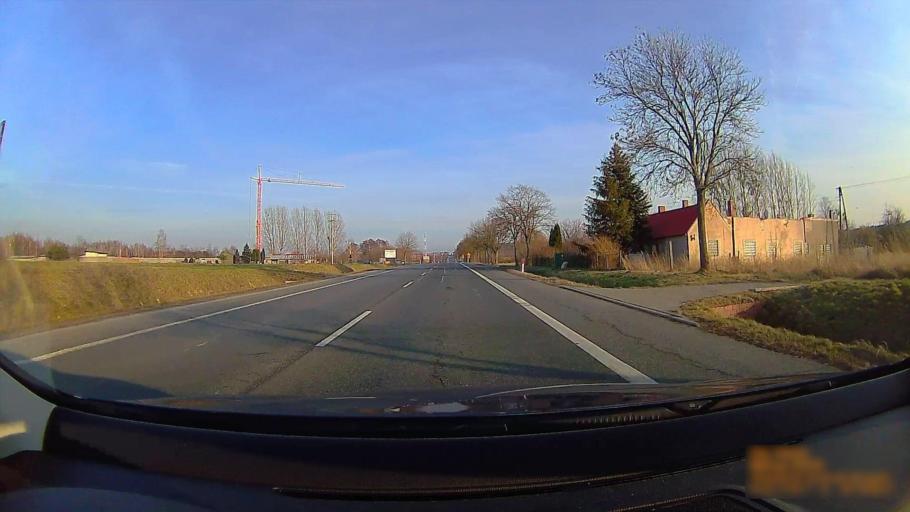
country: PL
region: Greater Poland Voivodeship
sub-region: Konin
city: Konin
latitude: 52.1917
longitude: 18.3276
